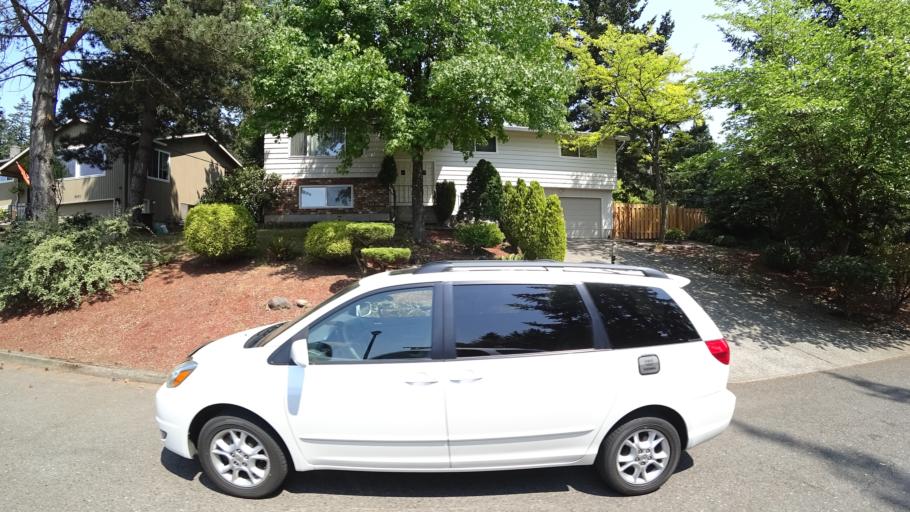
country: US
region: Oregon
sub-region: Clackamas County
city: Happy Valley
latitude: 45.4506
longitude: -122.5601
